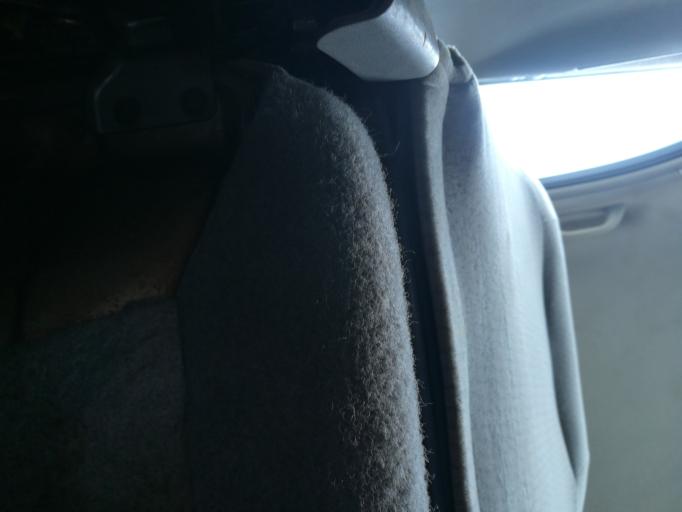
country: NG
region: Lagos
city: Ikoyi
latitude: 6.4435
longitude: 3.4253
